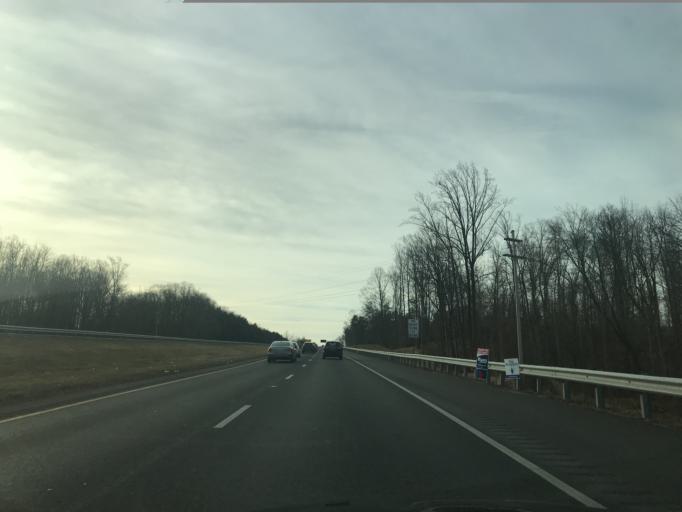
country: US
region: Maryland
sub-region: Prince George's County
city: Brandywine
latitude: 38.7242
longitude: -76.8811
